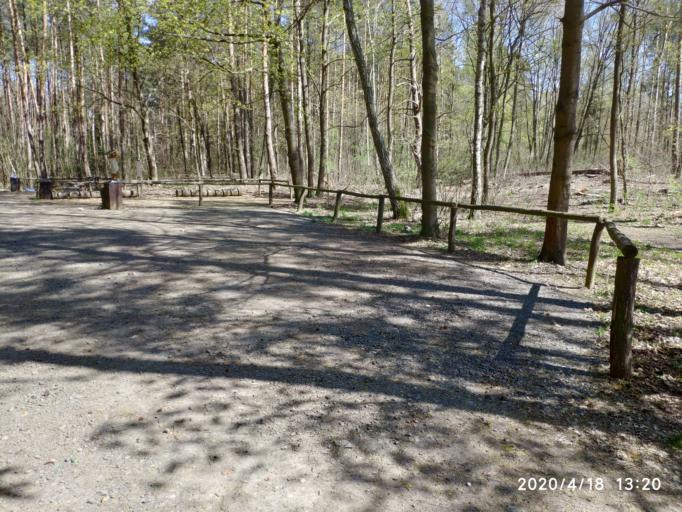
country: PL
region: Lubusz
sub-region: Powiat zielonogorski
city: Sulechow
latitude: 52.0919
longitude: 15.6704
